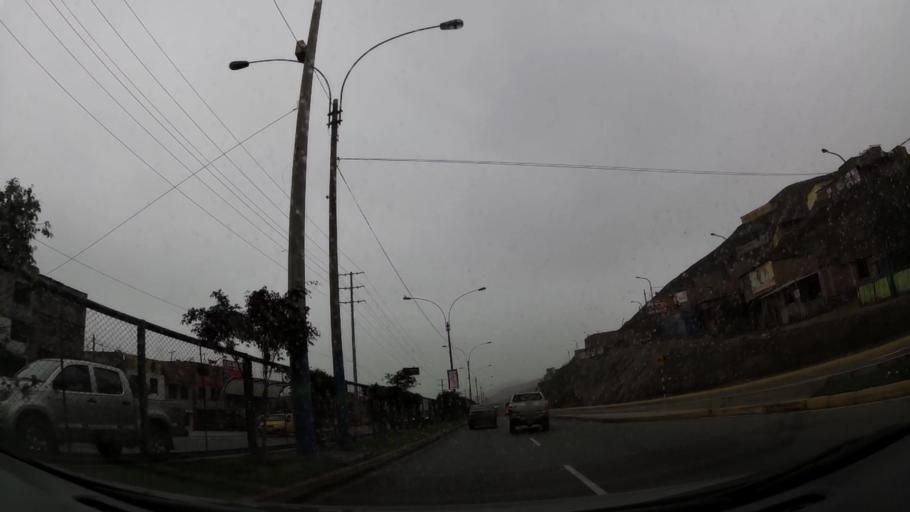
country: PE
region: Lima
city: Ventanilla
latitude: -11.8957
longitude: -77.1267
